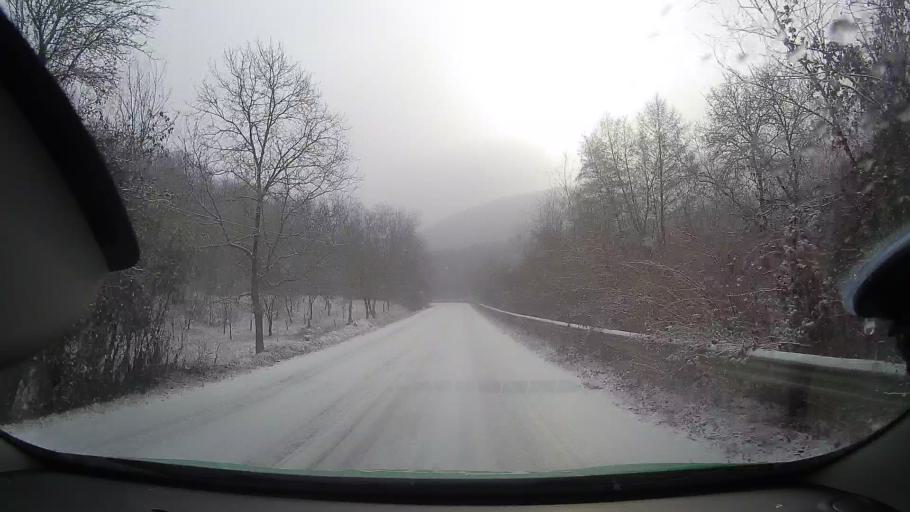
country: RO
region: Alba
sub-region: Comuna Livezile
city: Livezile
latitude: 46.3537
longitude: 23.6183
